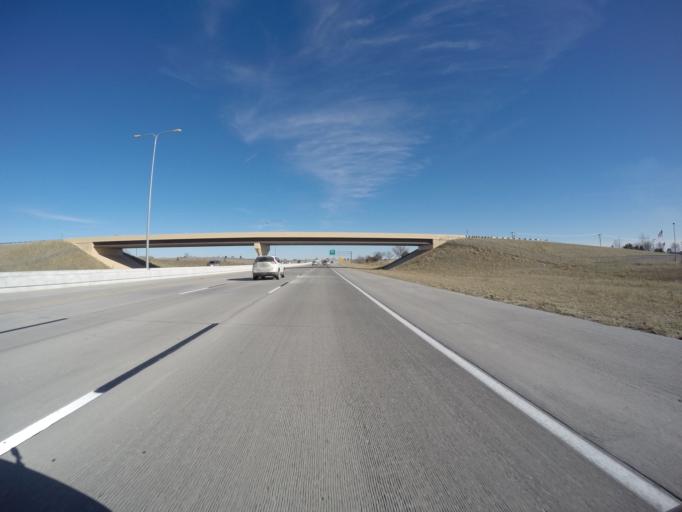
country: US
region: Nebraska
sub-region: Lancaster County
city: Lincoln
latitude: 40.8185
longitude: -96.7973
